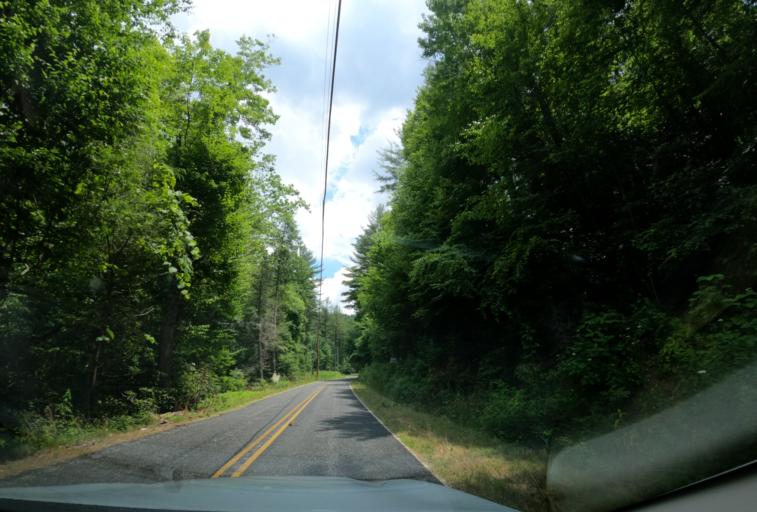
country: US
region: North Carolina
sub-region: Haywood County
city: Hazelwood
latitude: 35.4054
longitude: -82.9012
